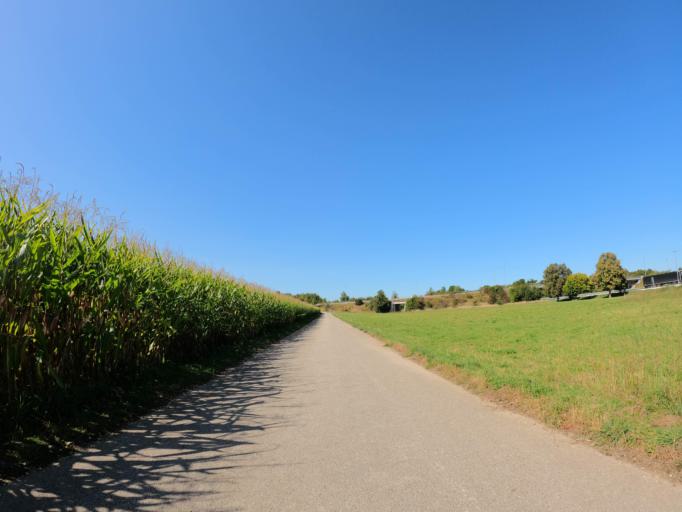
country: DE
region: Bavaria
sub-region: Upper Bavaria
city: Pasing
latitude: 48.1703
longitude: 11.4465
